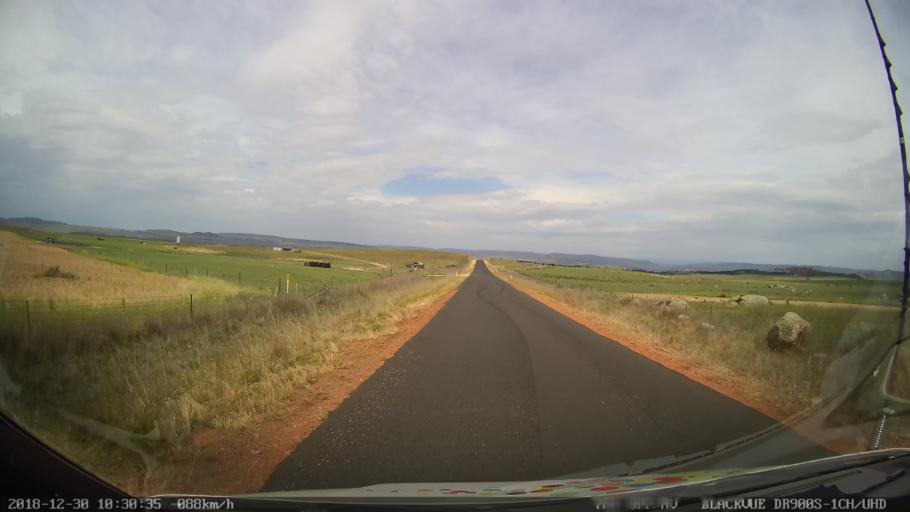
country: AU
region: New South Wales
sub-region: Snowy River
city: Berridale
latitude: -36.5042
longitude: 148.8927
